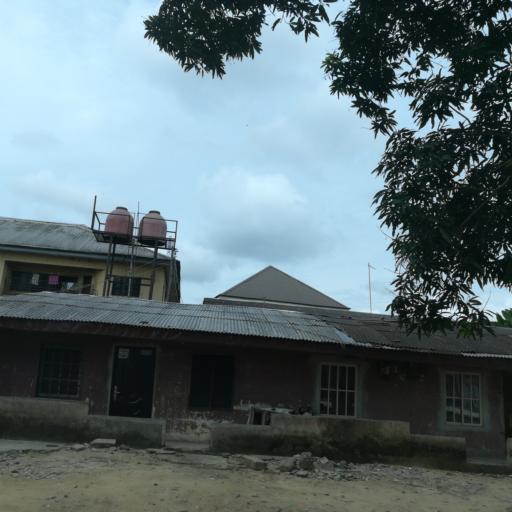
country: NG
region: Rivers
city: Port Harcourt
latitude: 4.7939
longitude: 7.0252
